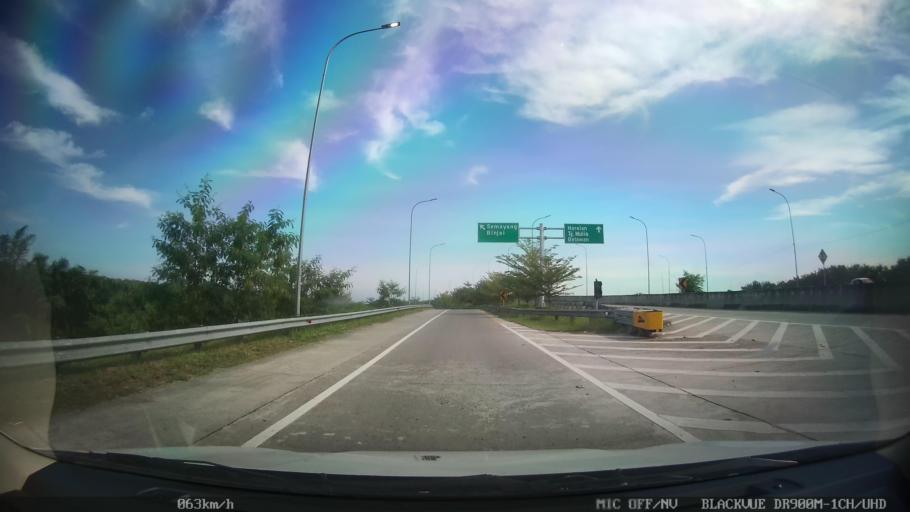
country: ID
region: North Sumatra
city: Medan
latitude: 3.6346
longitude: 98.6363
